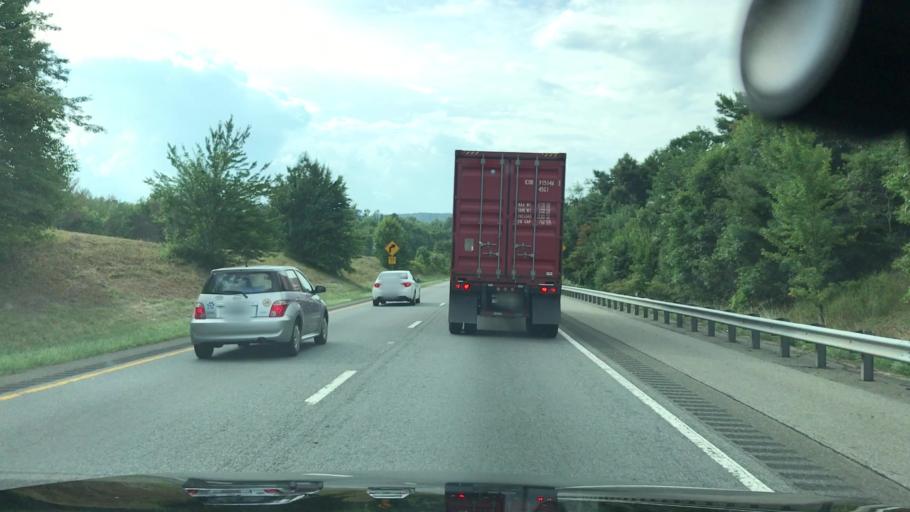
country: US
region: Virginia
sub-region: Carroll County
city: Woodlawn
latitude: 36.8048
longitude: -80.8503
